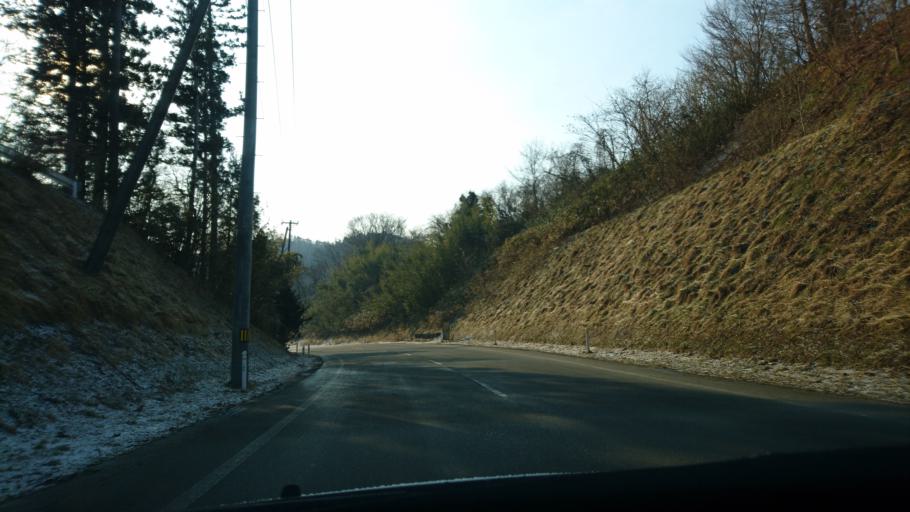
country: JP
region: Iwate
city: Ichinoseki
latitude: 38.9211
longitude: 141.3517
